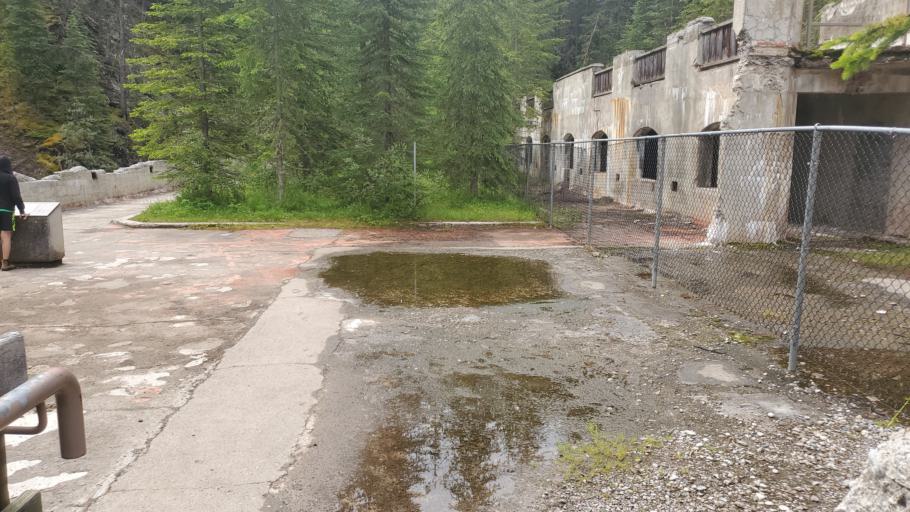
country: CA
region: Alberta
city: Hinton
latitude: 53.1261
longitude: -117.7750
